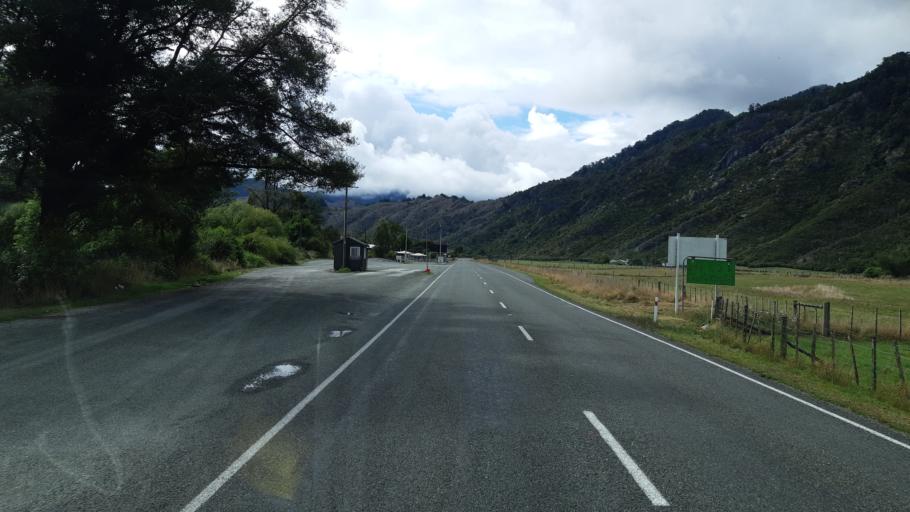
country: NZ
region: West Coast
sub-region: Buller District
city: Westport
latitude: -41.7964
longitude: 172.3473
